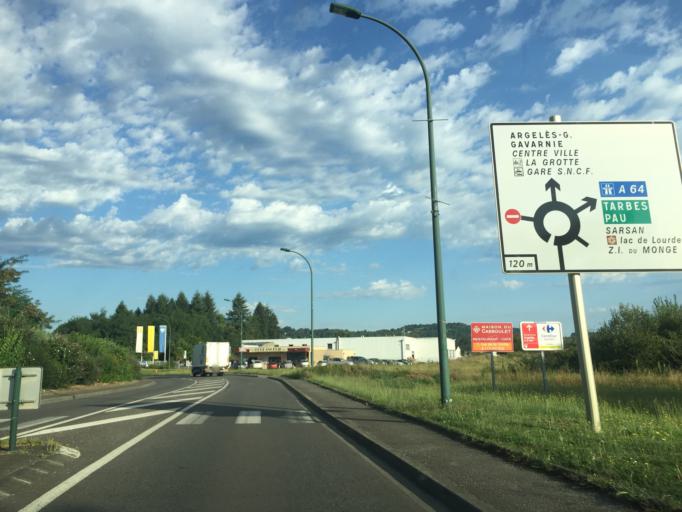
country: FR
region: Midi-Pyrenees
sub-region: Departement des Hautes-Pyrenees
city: Lourdes
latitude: 43.0969
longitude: -0.0265
